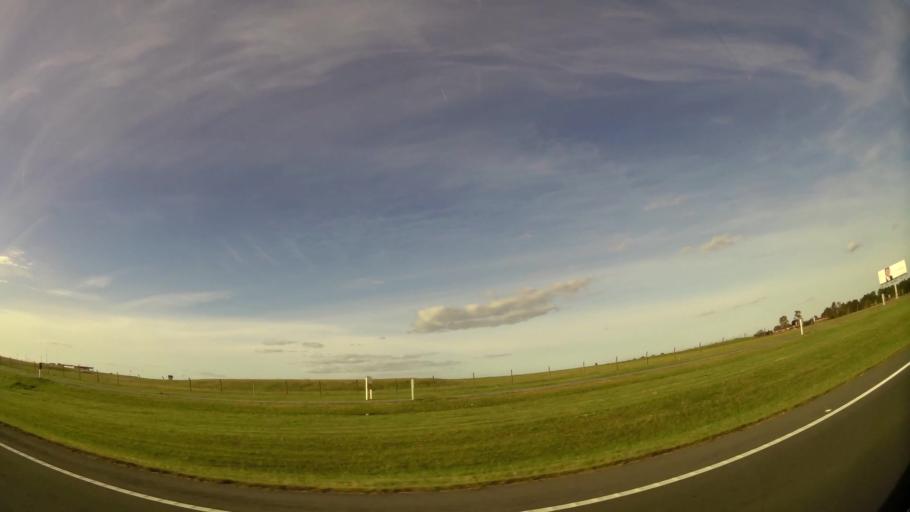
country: UY
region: Maldonado
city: Maldonado
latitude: -34.8665
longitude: -55.0931
